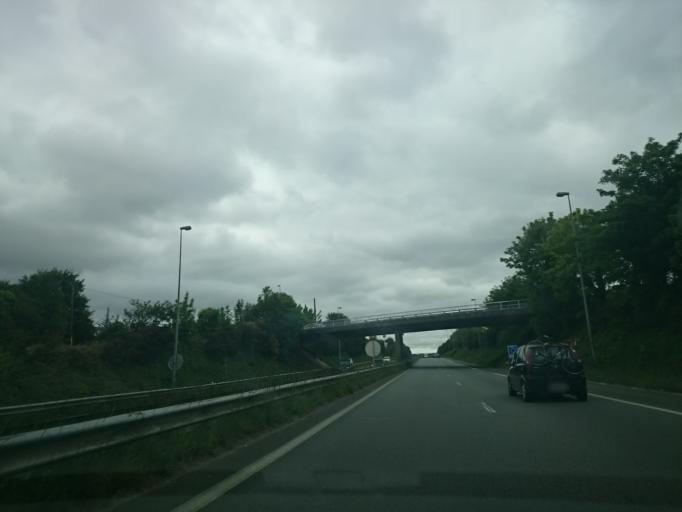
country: FR
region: Brittany
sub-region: Departement du Finistere
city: Brest
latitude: 48.4227
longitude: -4.4768
